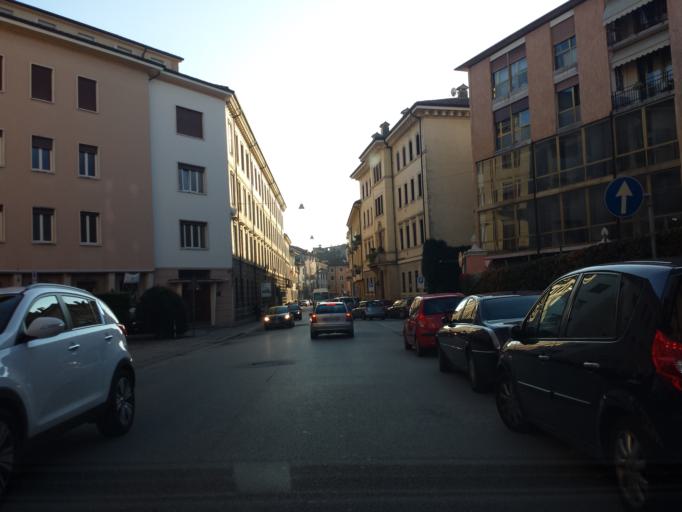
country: IT
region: Veneto
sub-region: Provincia di Vicenza
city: Vicenza
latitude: 45.5520
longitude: 11.5531
